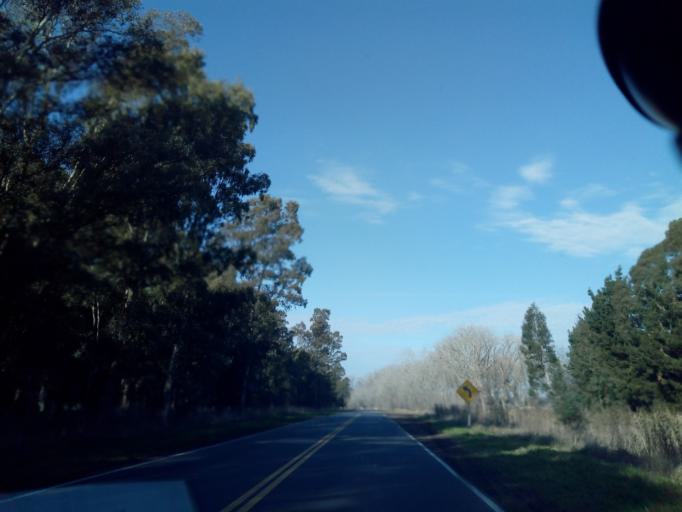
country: AR
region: Buenos Aires
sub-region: Partido de Tandil
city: Tandil
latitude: -37.3567
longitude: -58.8722
